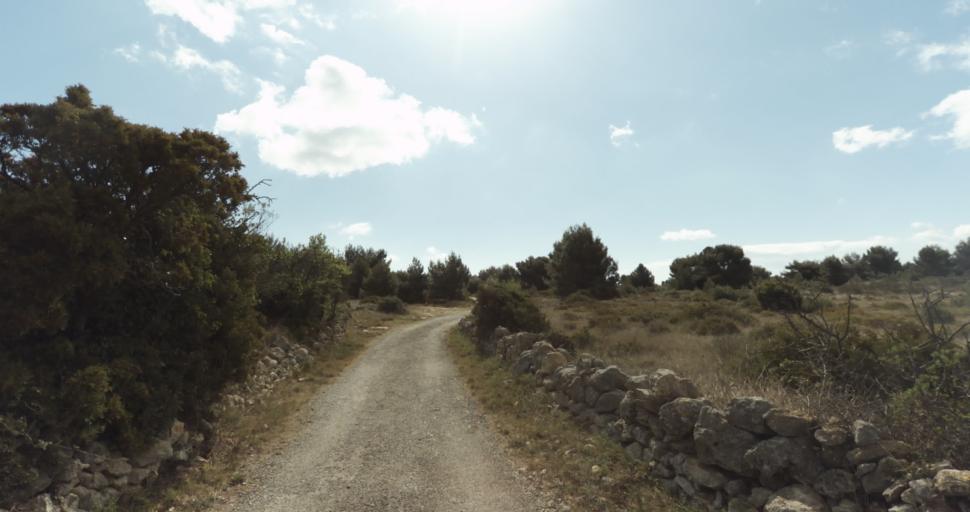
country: FR
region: Languedoc-Roussillon
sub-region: Departement de l'Aude
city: Leucate
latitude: 42.9196
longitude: 3.0479
